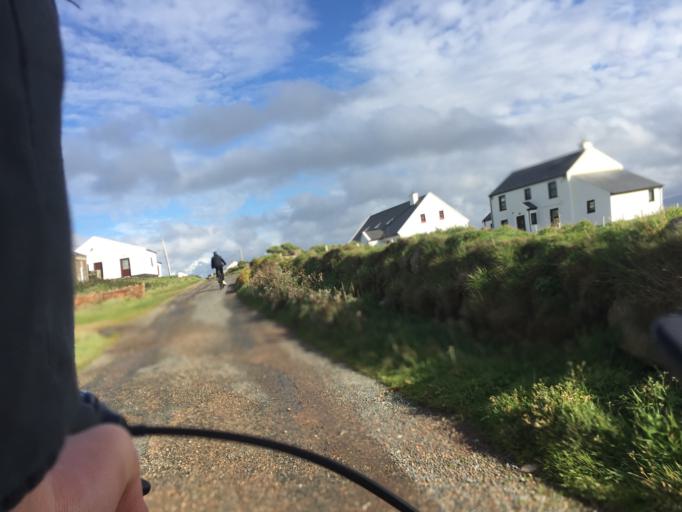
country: IE
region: Ulster
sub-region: County Donegal
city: Derrybeg
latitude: 55.2638
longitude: -8.2340
